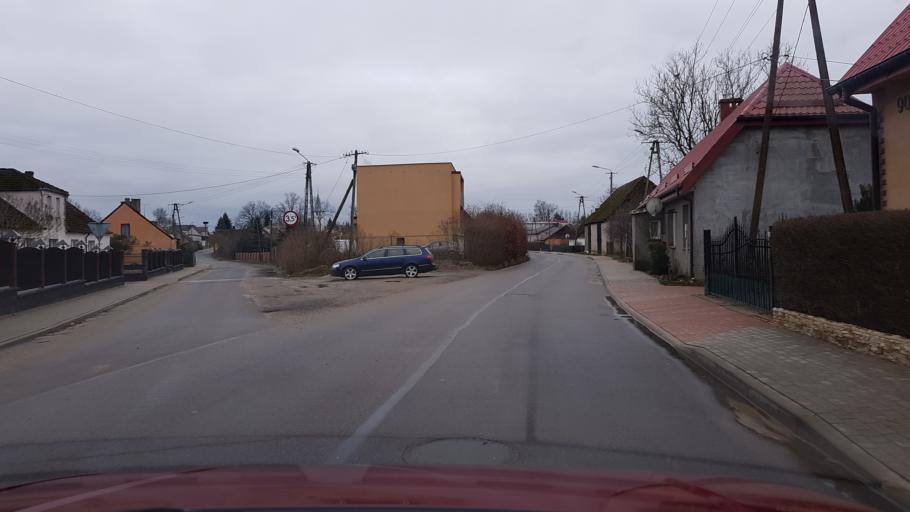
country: PL
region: West Pomeranian Voivodeship
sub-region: Powiat koszalinski
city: Mielno
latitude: 54.1364
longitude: 16.0379
